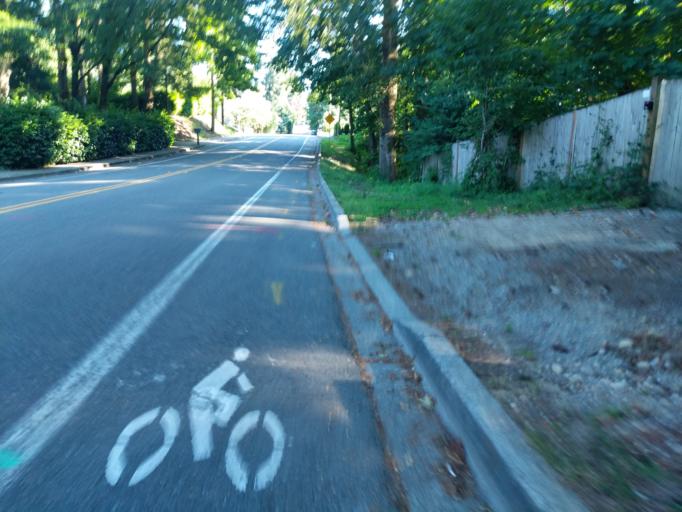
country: US
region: Washington
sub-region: King County
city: Bothell
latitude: 47.7767
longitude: -122.2018
